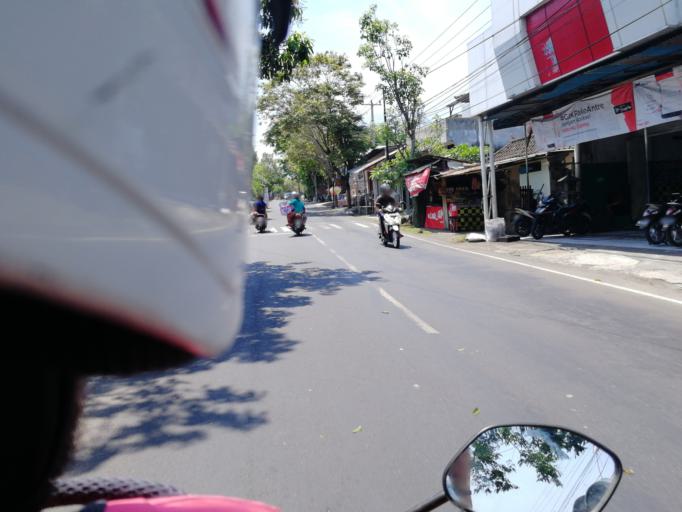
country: ID
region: Bali
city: Subagan
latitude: -8.4520
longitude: 115.5952
